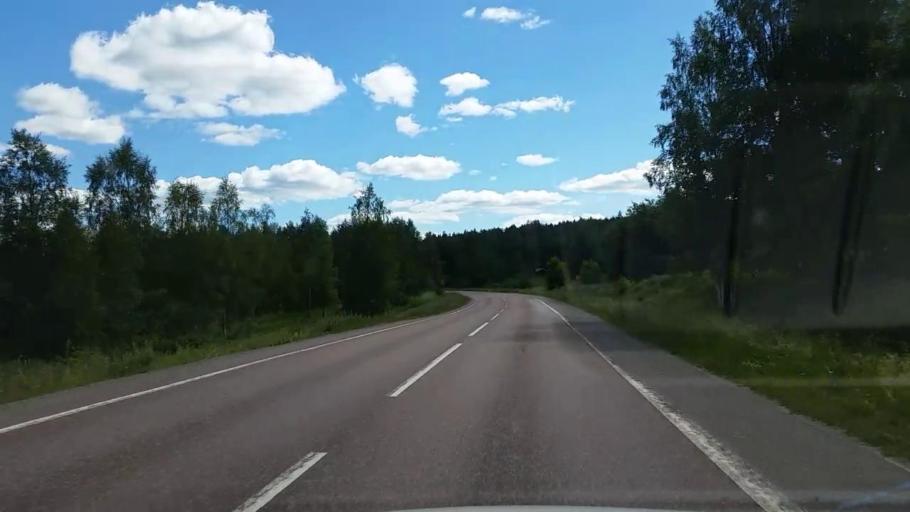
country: SE
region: Dalarna
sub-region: Faluns Kommun
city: Svardsjo
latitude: 60.8526
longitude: 15.7524
